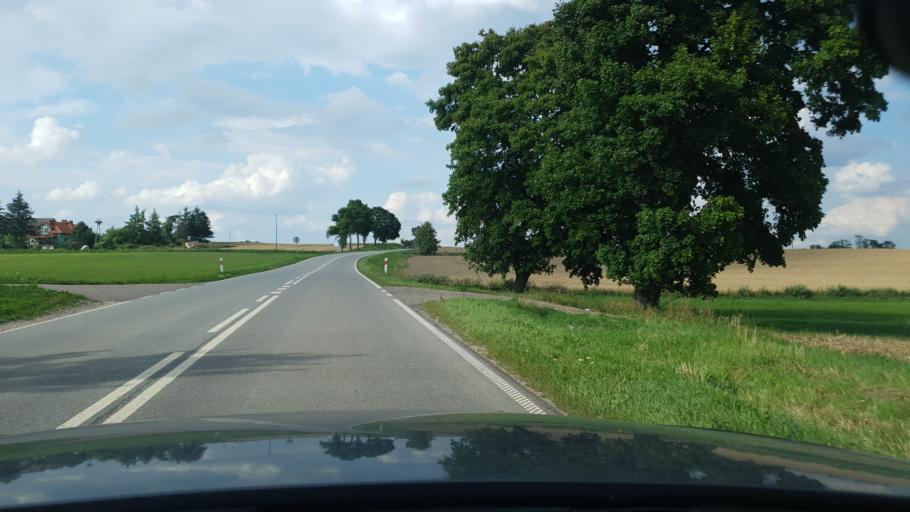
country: PL
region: Kujawsko-Pomorskie
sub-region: Powiat grudziadzki
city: Radzyn Chelminski
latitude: 53.3634
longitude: 18.9351
